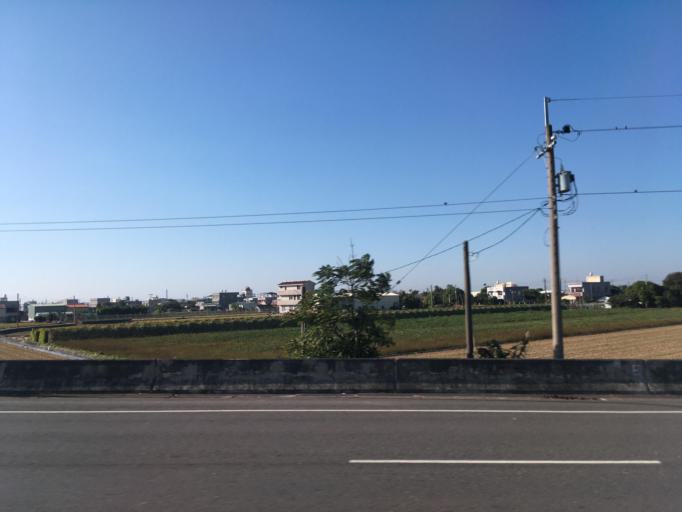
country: TW
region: Taiwan
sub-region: Chiayi
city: Taibao
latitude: 23.4307
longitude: 120.3203
